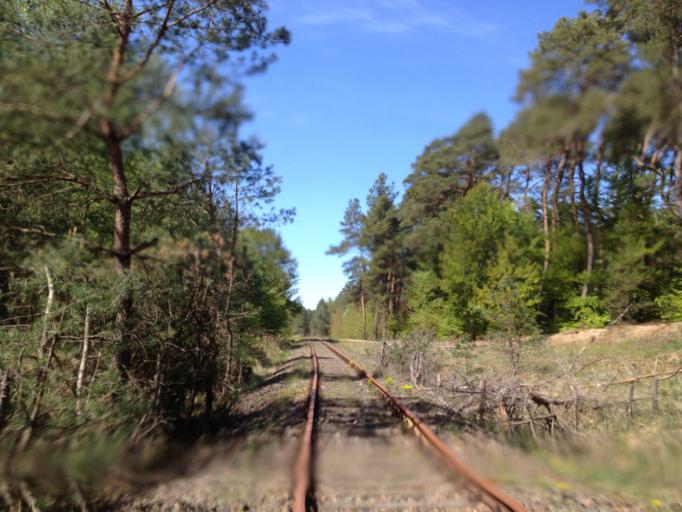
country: DE
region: Brandenburg
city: Lychen
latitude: 53.1658
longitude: 13.3719
